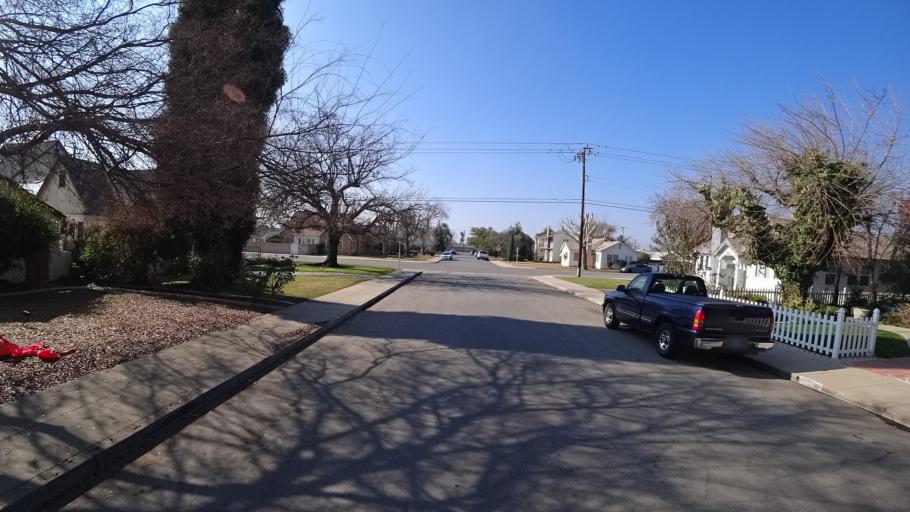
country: US
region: California
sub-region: Kern County
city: Bakersfield
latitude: 35.3893
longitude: -118.9987
